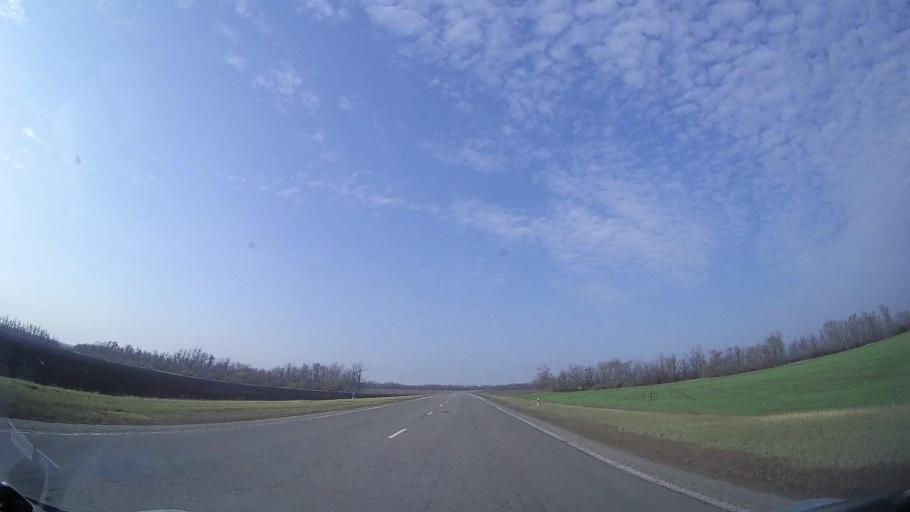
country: RU
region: Rostov
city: Tselina
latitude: 46.5131
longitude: 41.0298
